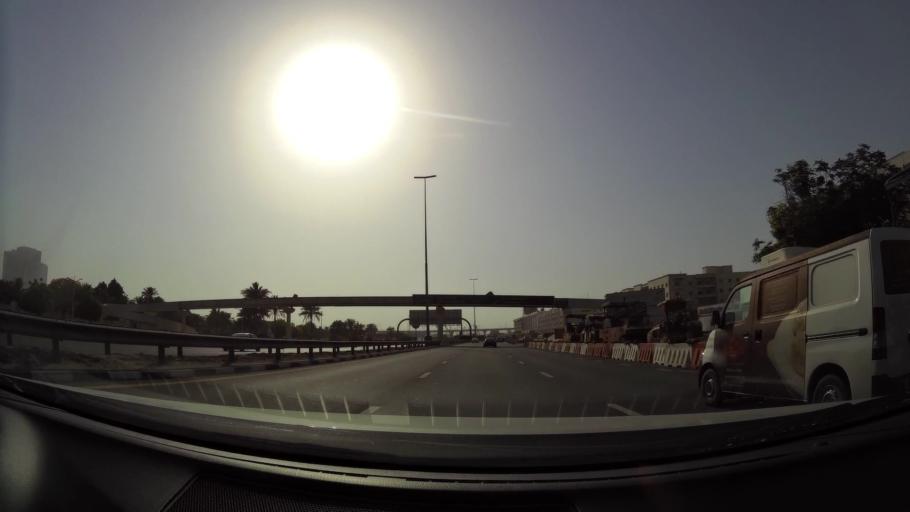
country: AE
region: Ash Shariqah
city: Sharjah
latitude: 25.2368
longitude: 55.3005
